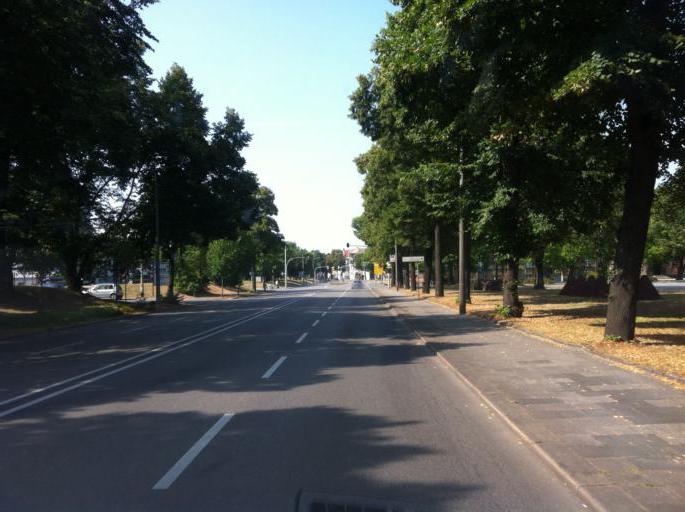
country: DE
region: Saxony
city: Zwickau
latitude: 50.7209
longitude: 12.4879
